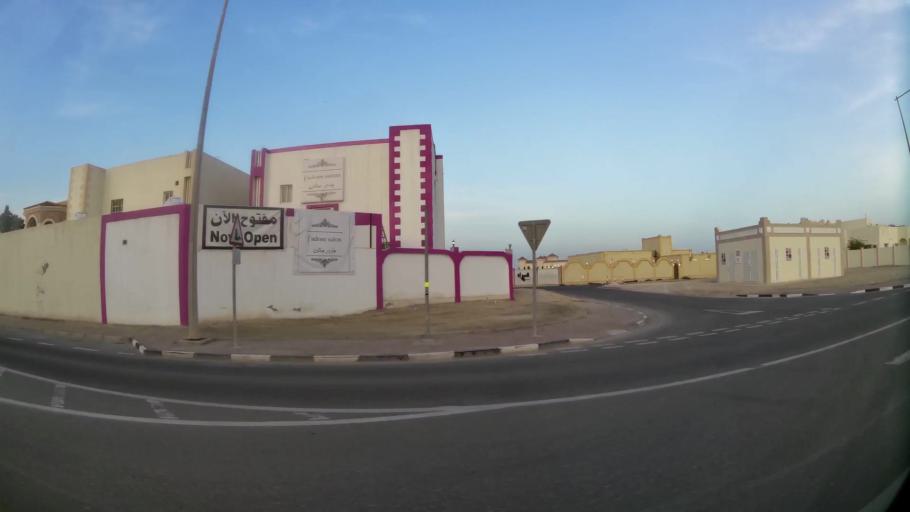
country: QA
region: Al Wakrah
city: Al Wakrah
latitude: 25.1884
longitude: 51.6068
